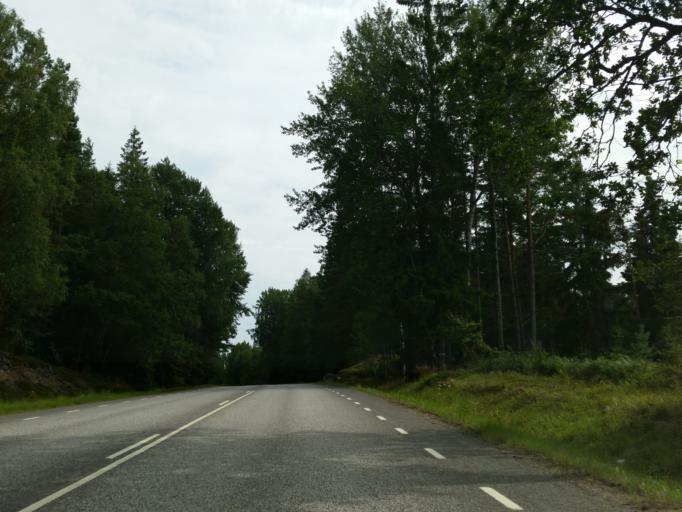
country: SE
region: Soedermanland
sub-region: Strangnas Kommun
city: Mariefred
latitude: 59.2386
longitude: 17.1945
